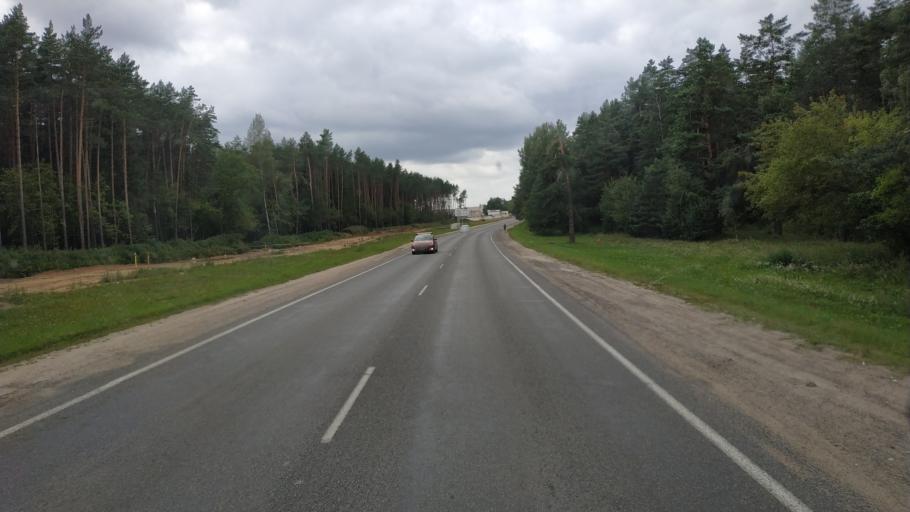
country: BY
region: Mogilev
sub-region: Mahilyowski Rayon
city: Veyno
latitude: 53.8777
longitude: 30.4172
